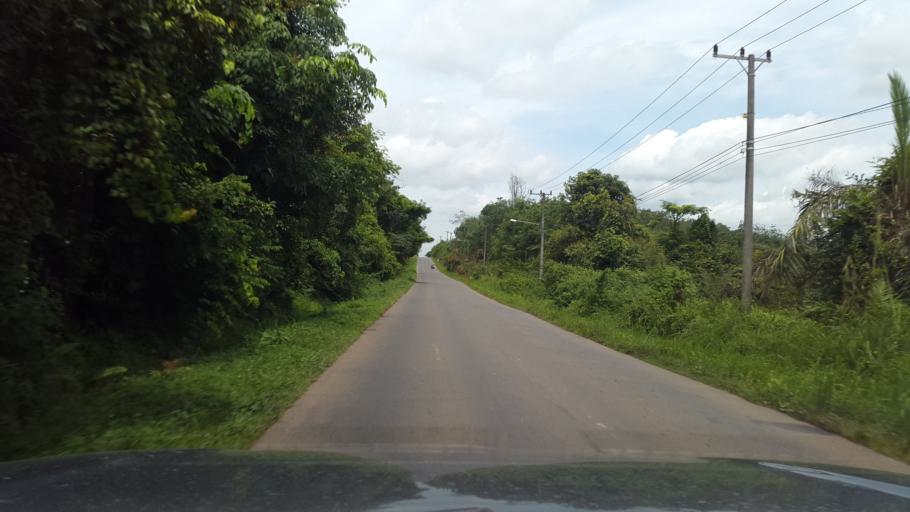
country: ID
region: South Sumatra
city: Gunungmegang Dalam
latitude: -3.3775
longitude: 103.9481
